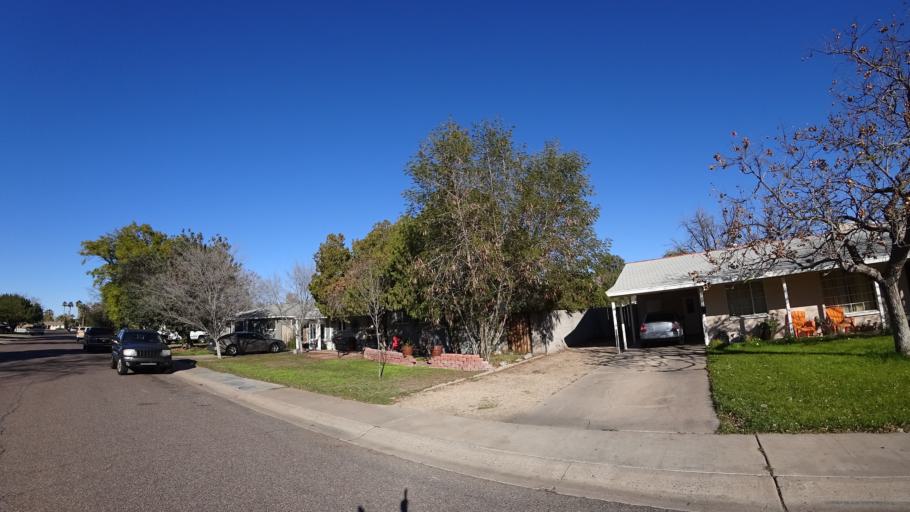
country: US
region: Arizona
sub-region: Maricopa County
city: Phoenix
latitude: 33.5205
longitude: -112.0528
